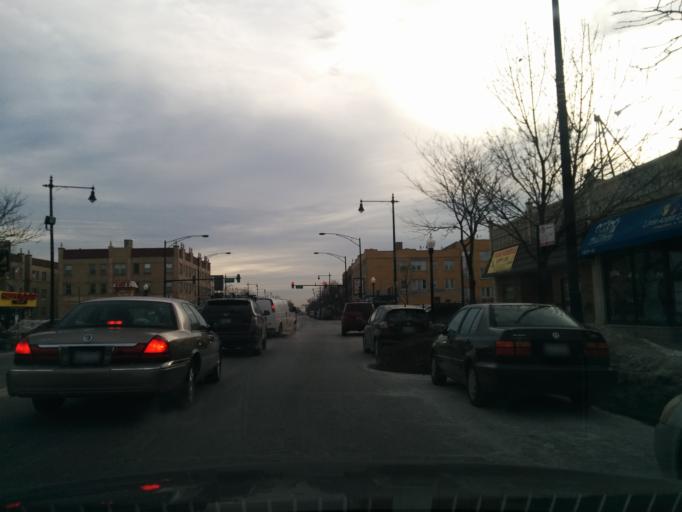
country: US
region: Illinois
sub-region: Cook County
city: Harwood Heights
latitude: 41.9530
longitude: -87.7731
